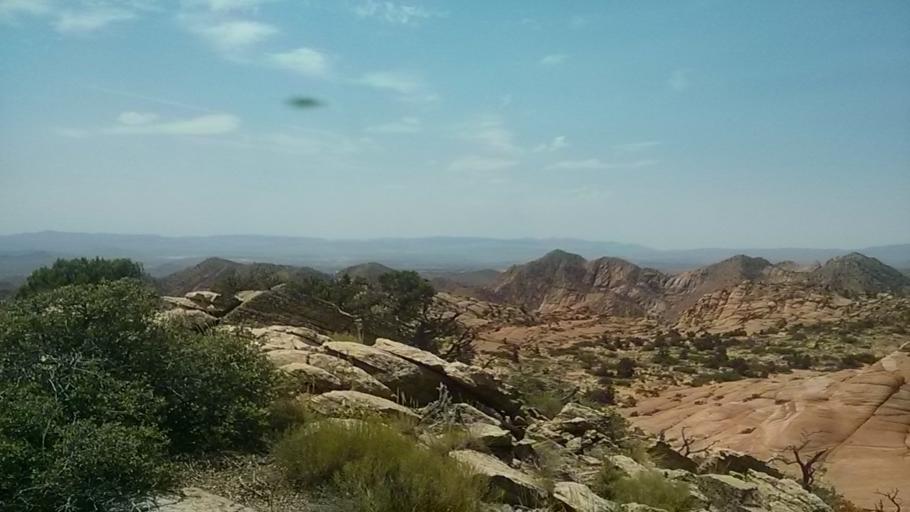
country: US
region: Utah
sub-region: Washington County
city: Washington
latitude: 37.2181
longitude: -113.4615
